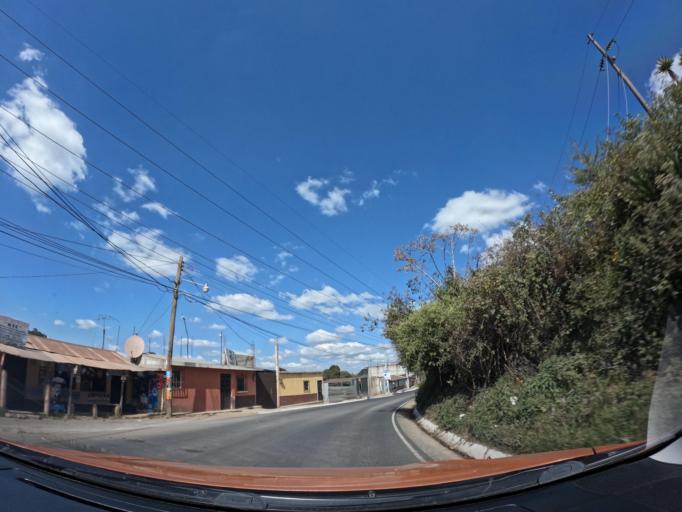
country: GT
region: Chimaltenango
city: Patzun
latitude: 14.6611
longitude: -91.0186
